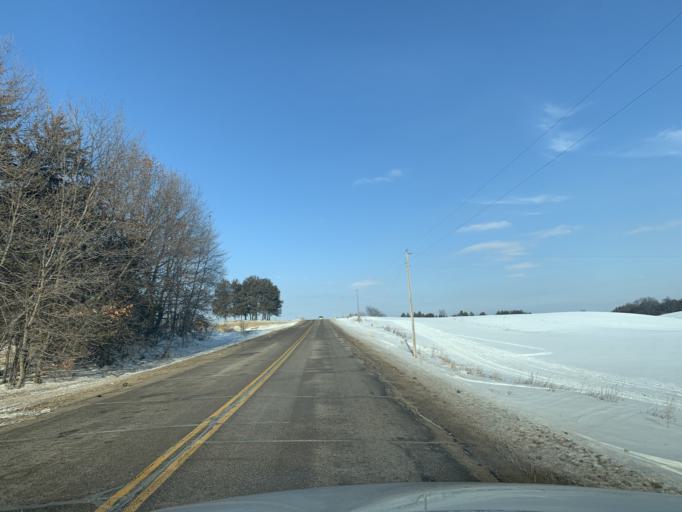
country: US
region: Minnesota
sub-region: Wright County
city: Buffalo
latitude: 45.2008
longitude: -93.8271
